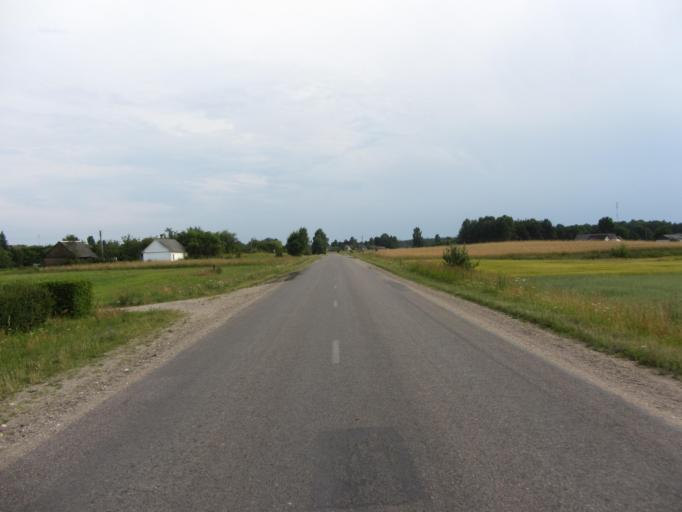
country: LT
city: Veisiejai
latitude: 54.0126
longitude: 23.6553
